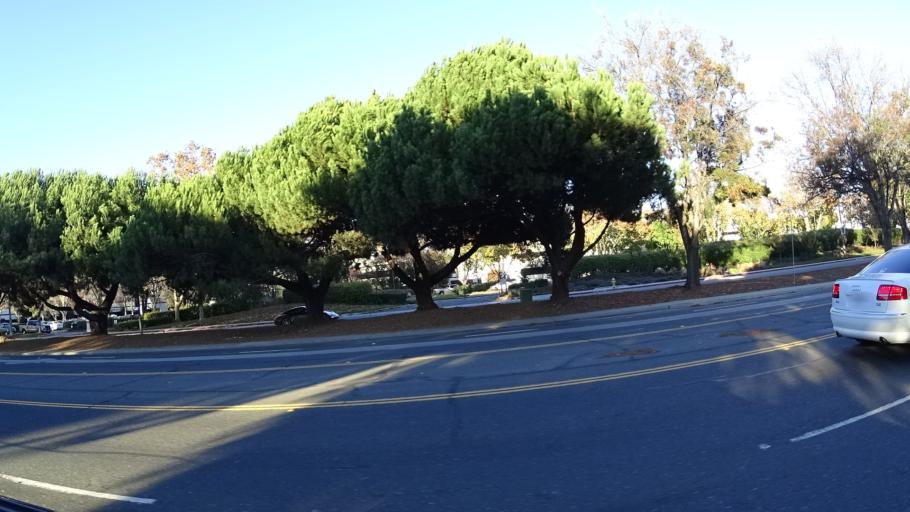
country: US
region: California
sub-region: Santa Clara County
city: Santa Clara
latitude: 37.3553
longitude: -121.9300
